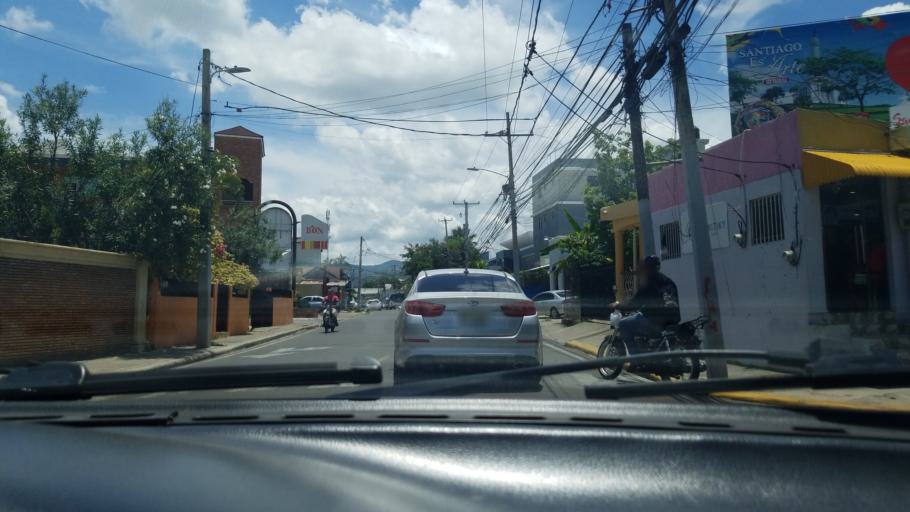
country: DO
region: Santiago
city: Santiago de los Caballeros
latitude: 19.4749
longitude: -70.6859
